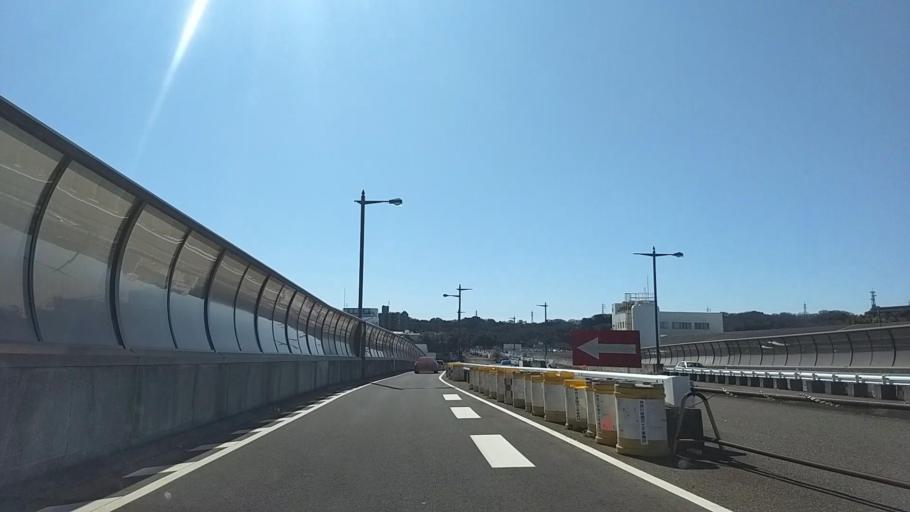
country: JP
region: Kanagawa
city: Fujisawa
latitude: 35.3357
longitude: 139.5015
